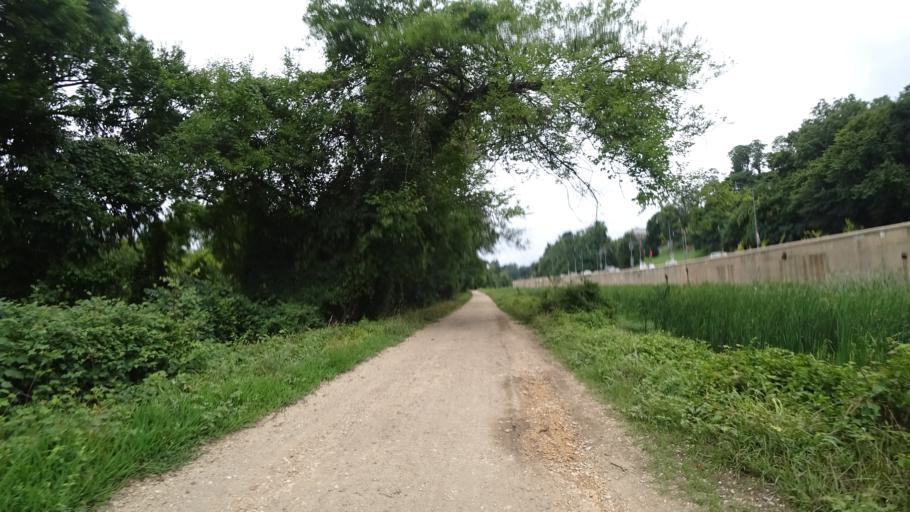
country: US
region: Washington, D.C.
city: Washington, D.C.
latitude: 38.9051
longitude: -77.0733
